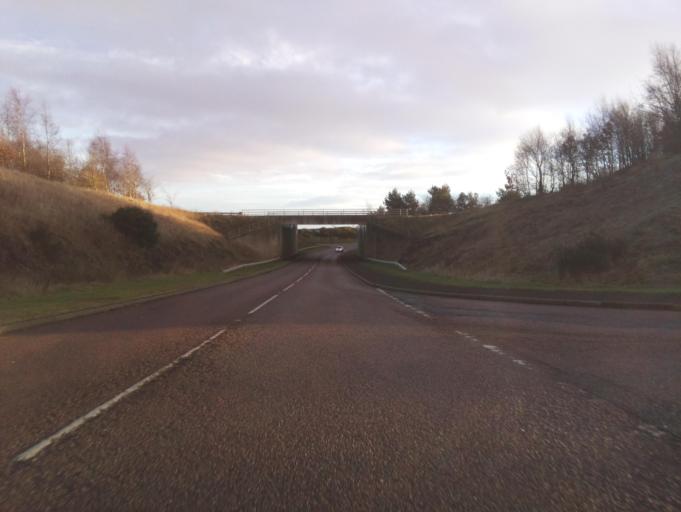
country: GB
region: Scotland
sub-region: Fife
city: Tayport
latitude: 56.4994
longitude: -2.8059
